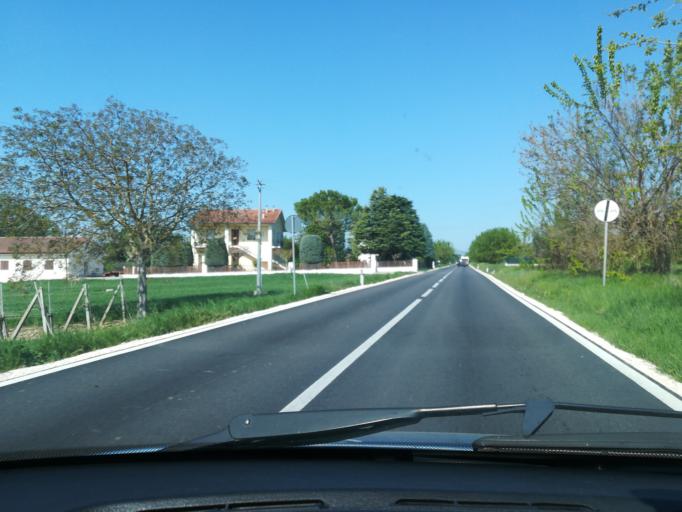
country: IT
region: The Marches
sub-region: Provincia di Macerata
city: Villa Potenza
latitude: 43.3245
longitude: 13.4122
